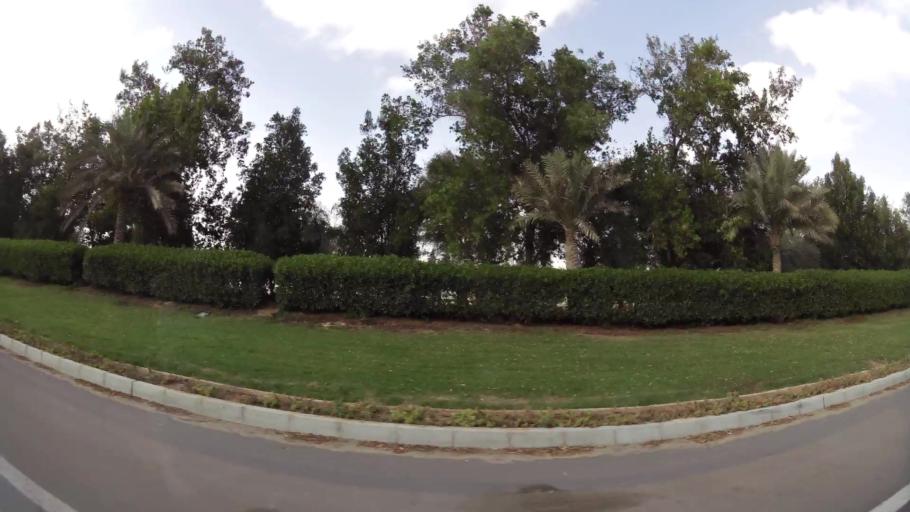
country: AE
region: Abu Dhabi
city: Abu Dhabi
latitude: 24.3922
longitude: 54.5461
